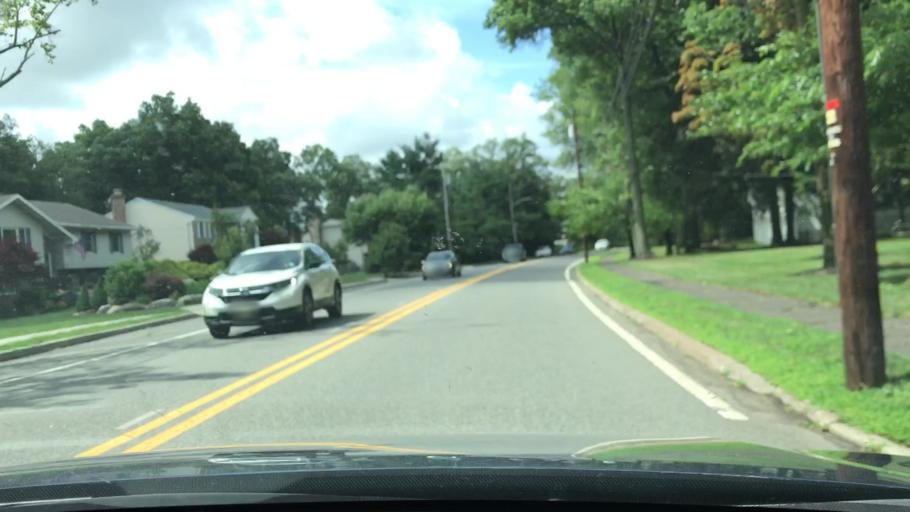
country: US
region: New Jersey
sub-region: Bergen County
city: Wyckoff
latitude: 41.0148
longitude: -74.1664
